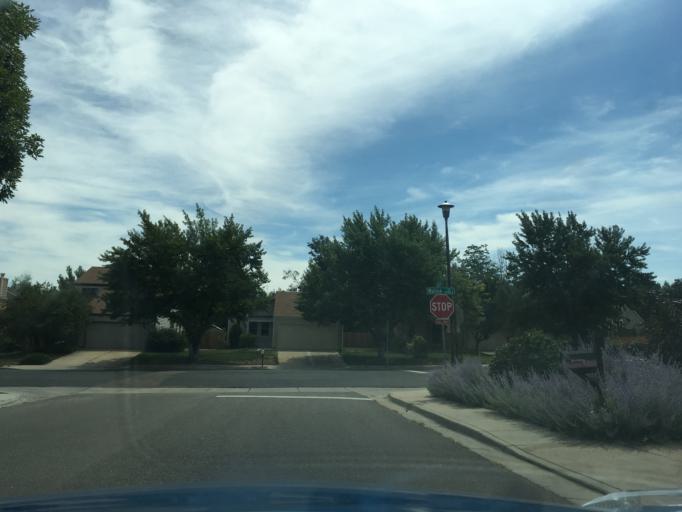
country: US
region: Colorado
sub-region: Adams County
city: Aurora
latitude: 39.7161
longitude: -104.8569
